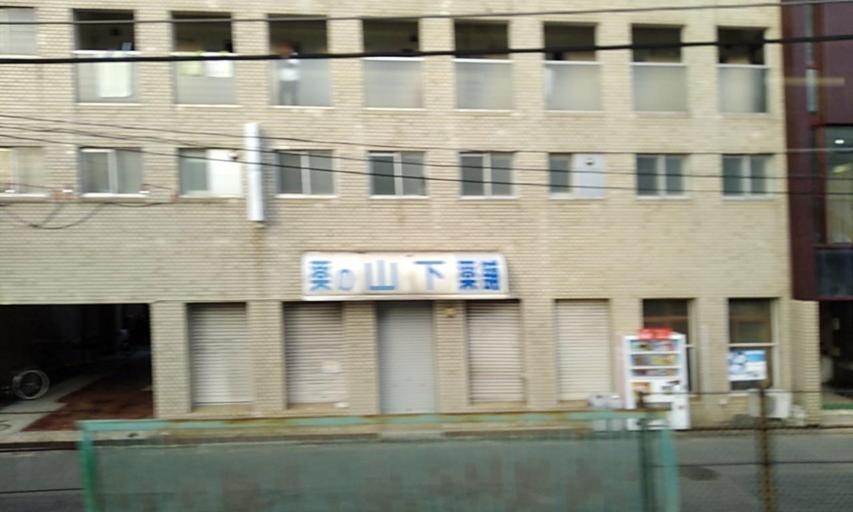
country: JP
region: Osaka
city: Sakai
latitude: 34.5641
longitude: 135.4941
